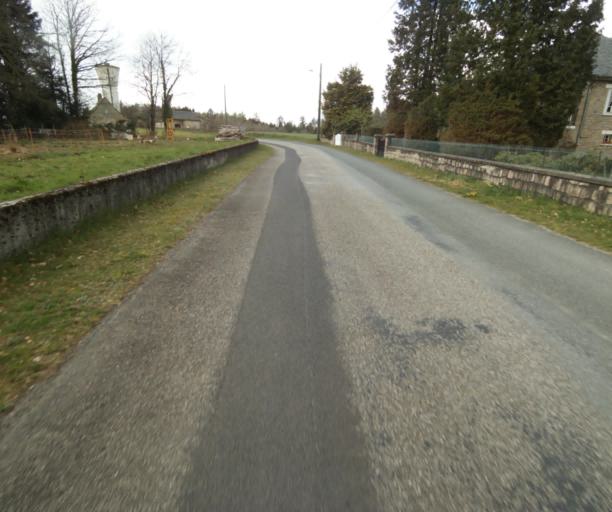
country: FR
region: Limousin
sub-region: Departement de la Correze
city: Correze
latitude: 45.2806
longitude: 1.9764
